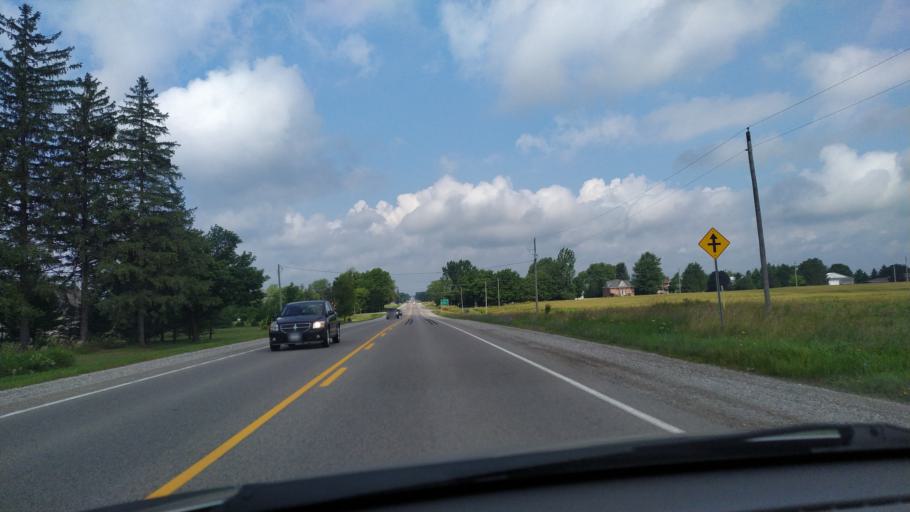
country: CA
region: Ontario
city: Stratford
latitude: 43.4285
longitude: -81.1087
